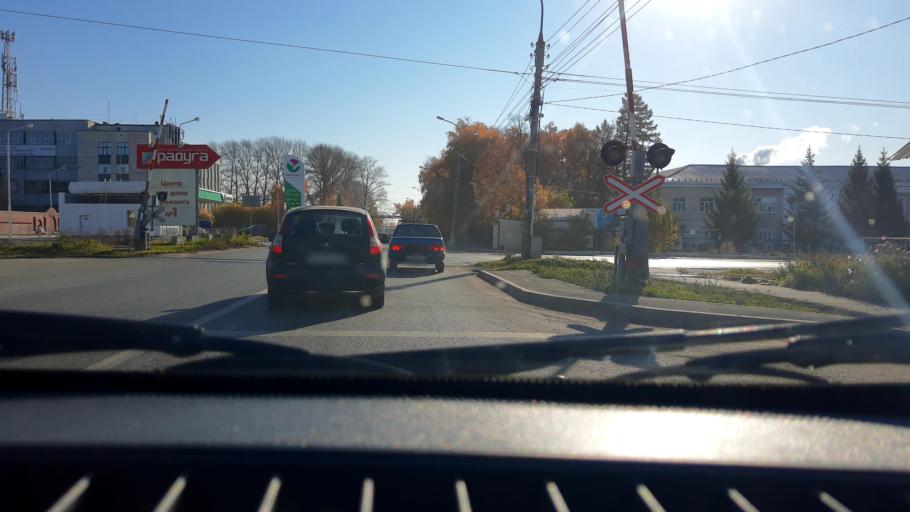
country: RU
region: Bashkortostan
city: Ufa
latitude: 54.8039
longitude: 56.0952
